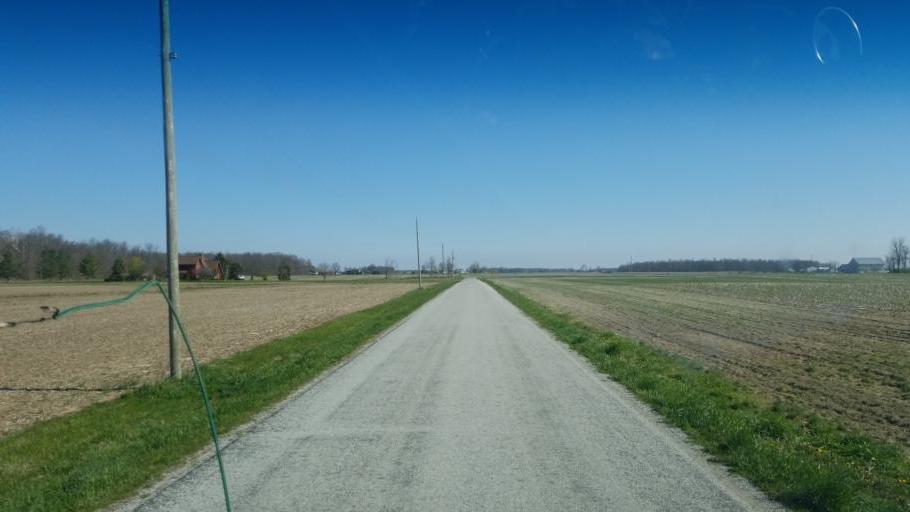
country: US
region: Ohio
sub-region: Hardin County
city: Kenton
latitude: 40.6776
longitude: -83.5617
